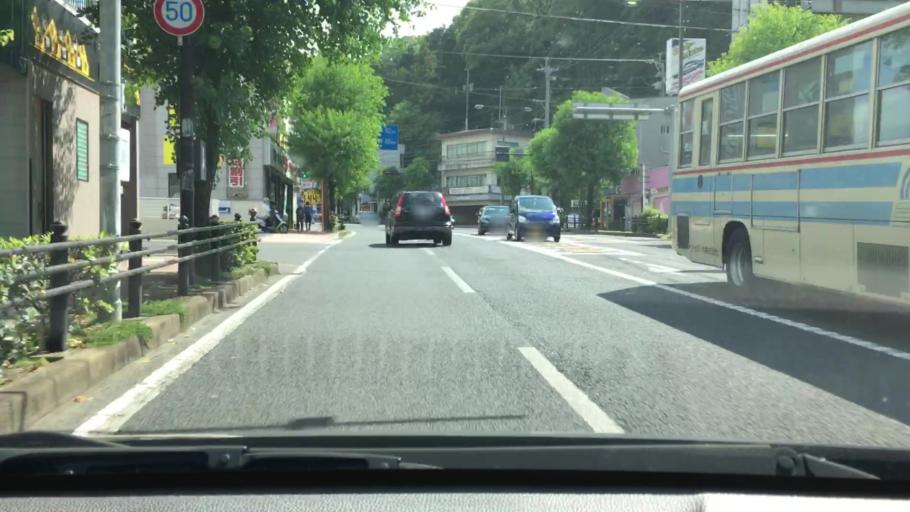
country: JP
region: Nagasaki
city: Sasebo
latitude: 33.2056
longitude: 129.7212
